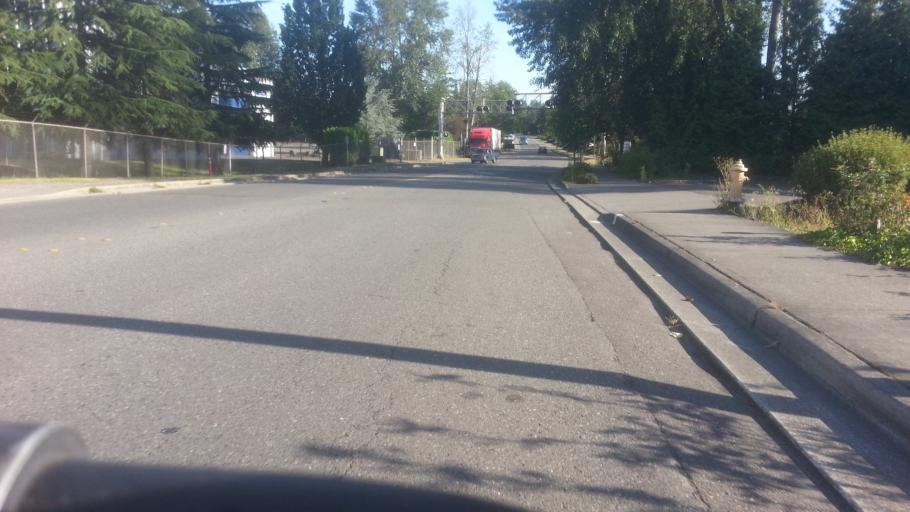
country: US
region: Washington
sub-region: King County
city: Bellevue
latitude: 47.6302
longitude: -122.1805
